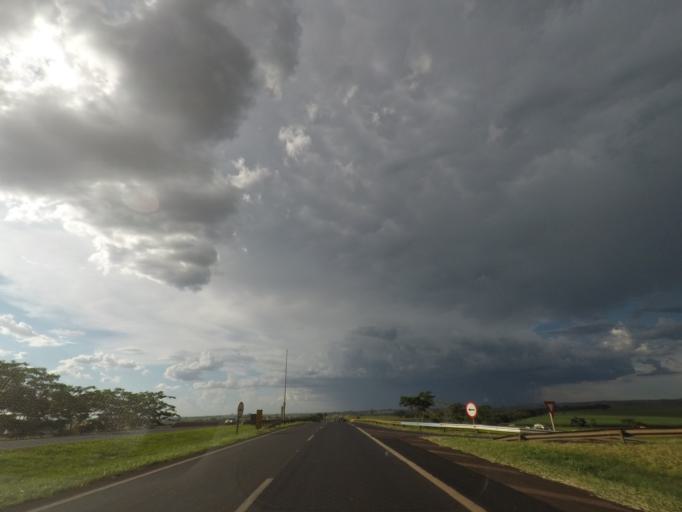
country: BR
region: Sao Paulo
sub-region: Jardinopolis
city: Jardinopolis
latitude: -21.0937
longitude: -47.7938
